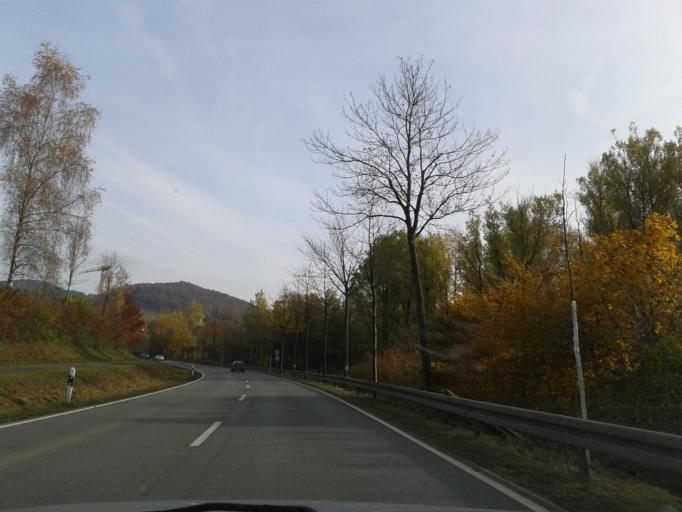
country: DE
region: North Rhine-Westphalia
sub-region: Regierungsbezirk Arnsberg
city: Bestwig
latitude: 51.3647
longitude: 8.4405
